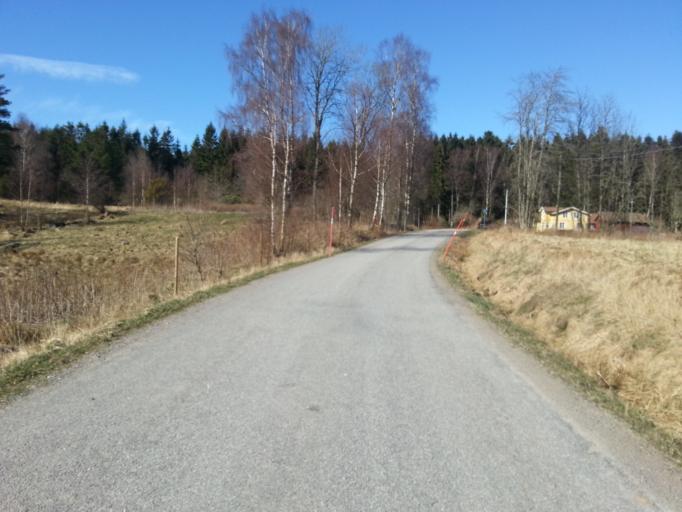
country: SE
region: Vaestra Goetaland
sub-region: Kungalvs Kommun
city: Kungalv
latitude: 57.9036
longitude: 11.9486
